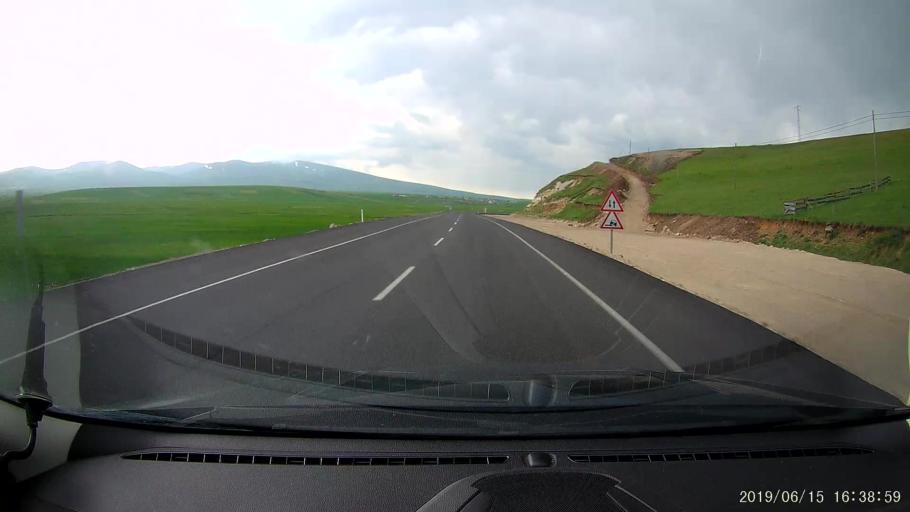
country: TR
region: Ardahan
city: Haskoy
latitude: 40.9875
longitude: 42.8928
